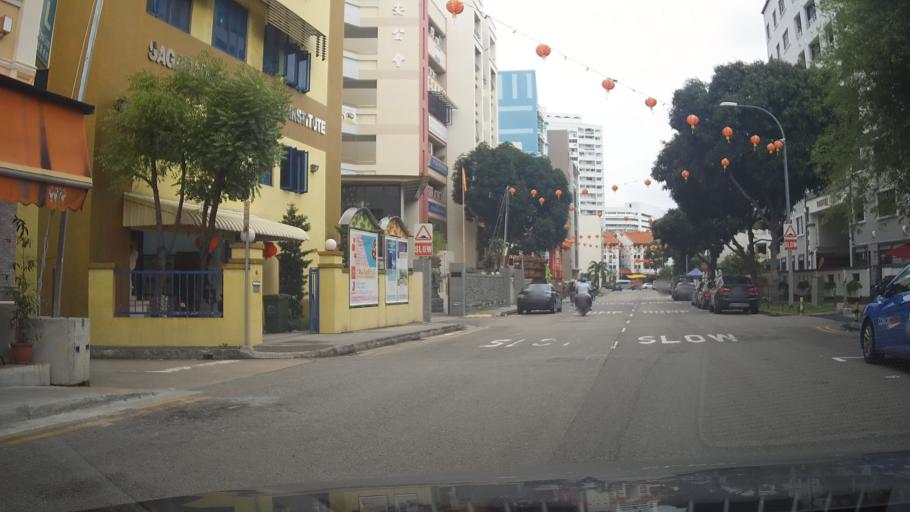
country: SG
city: Singapore
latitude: 1.3140
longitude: 103.8856
